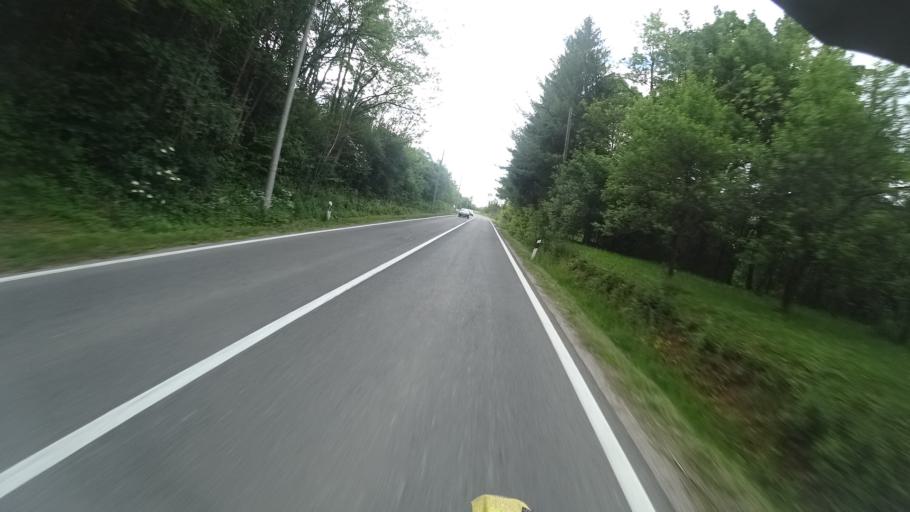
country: HR
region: Licko-Senjska
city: Gospic
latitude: 44.4962
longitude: 15.4588
